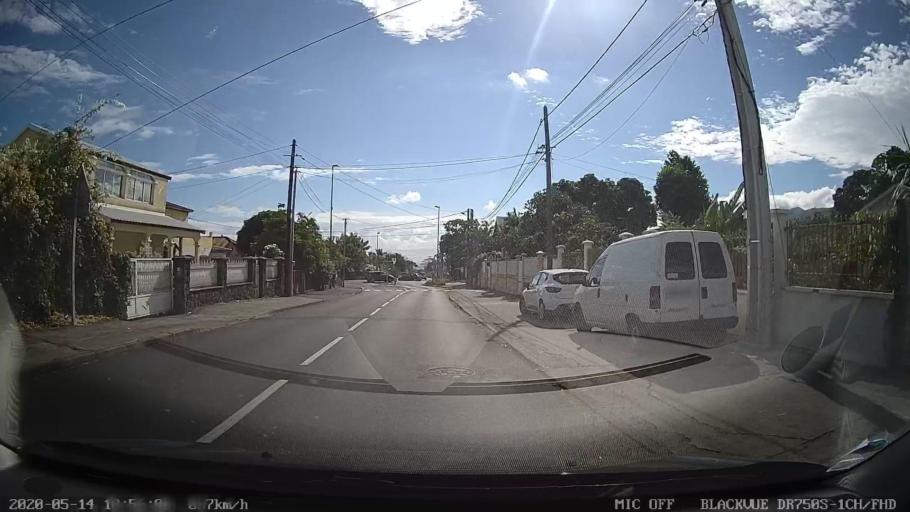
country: RE
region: Reunion
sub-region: Reunion
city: La Possession
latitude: -20.9601
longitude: 55.3215
